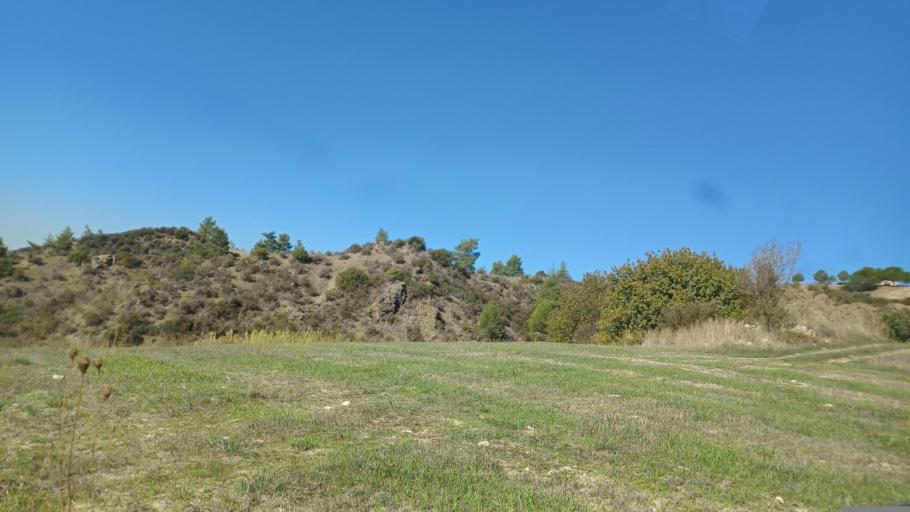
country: CY
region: Pafos
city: Polis
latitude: 35.0311
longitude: 32.4960
